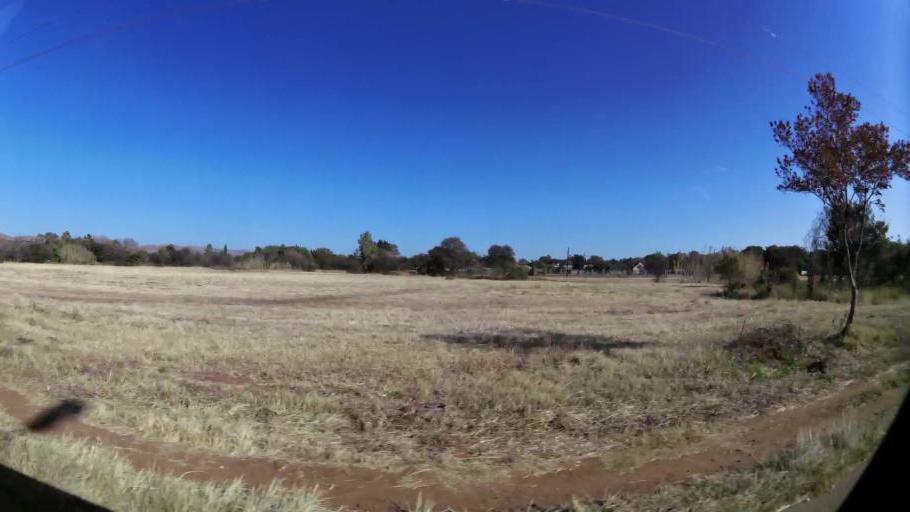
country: ZA
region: Gauteng
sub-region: City of Tshwane Metropolitan Municipality
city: Pretoria
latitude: -25.6626
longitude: 28.1322
